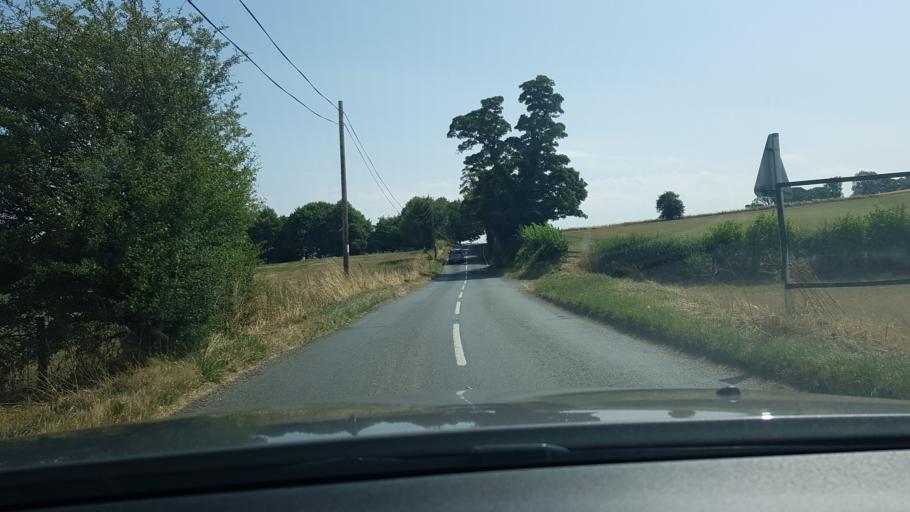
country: GB
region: England
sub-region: West Berkshire
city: Wickham
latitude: 51.4801
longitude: -1.4678
